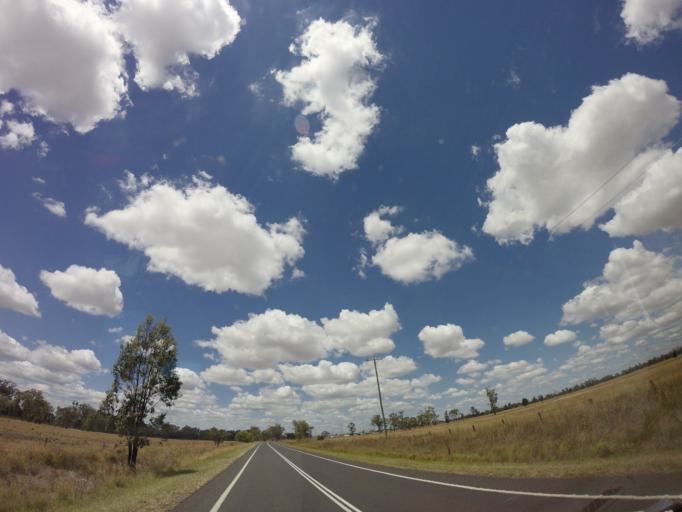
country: AU
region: Queensland
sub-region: Toowoomba
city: Oakey
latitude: -27.8755
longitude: 151.2355
